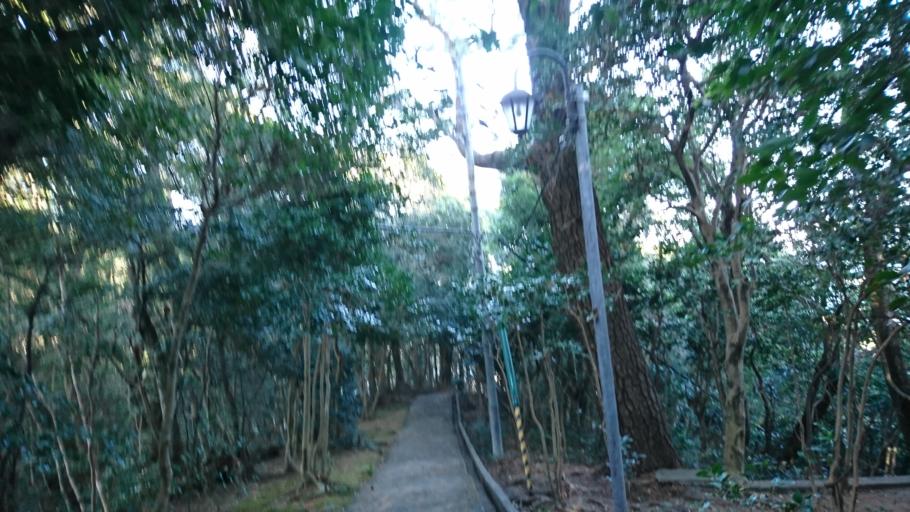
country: JP
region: Kochi
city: Kochi-shi
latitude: 33.4972
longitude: 133.5728
